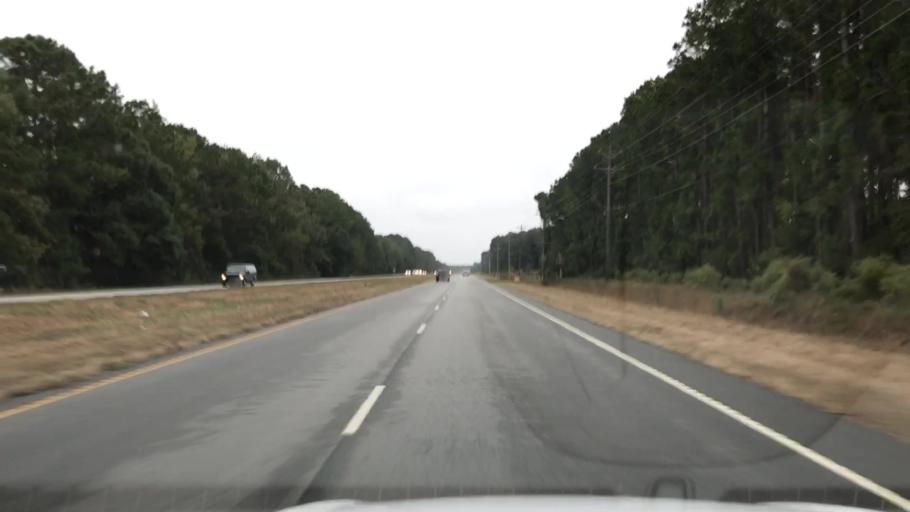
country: US
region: South Carolina
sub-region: Charleston County
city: Isle of Palms
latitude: 32.9046
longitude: -79.7276
